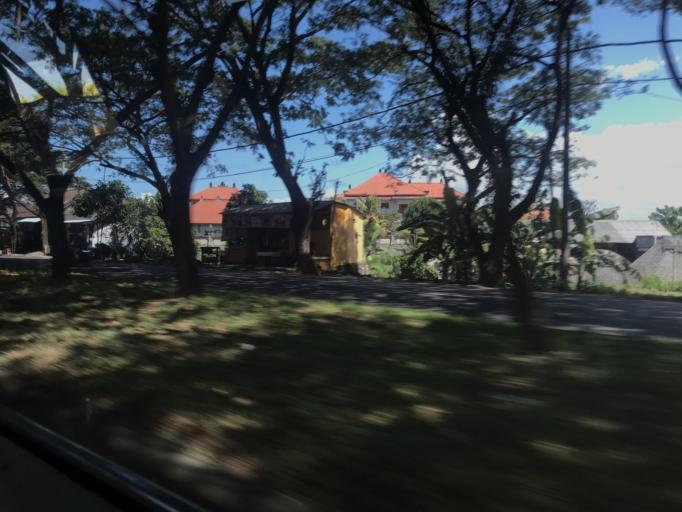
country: ID
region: Bali
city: Dawan
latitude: -8.5556
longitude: 115.4322
